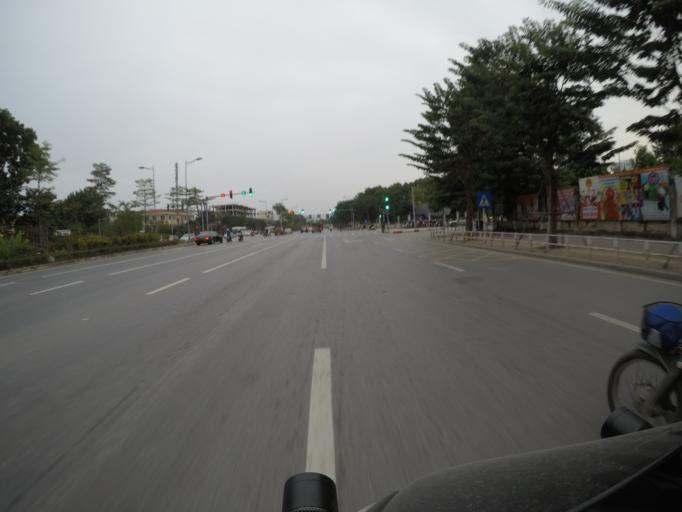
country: VN
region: Ha Noi
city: Tay Ho
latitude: 21.0654
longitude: 105.8061
